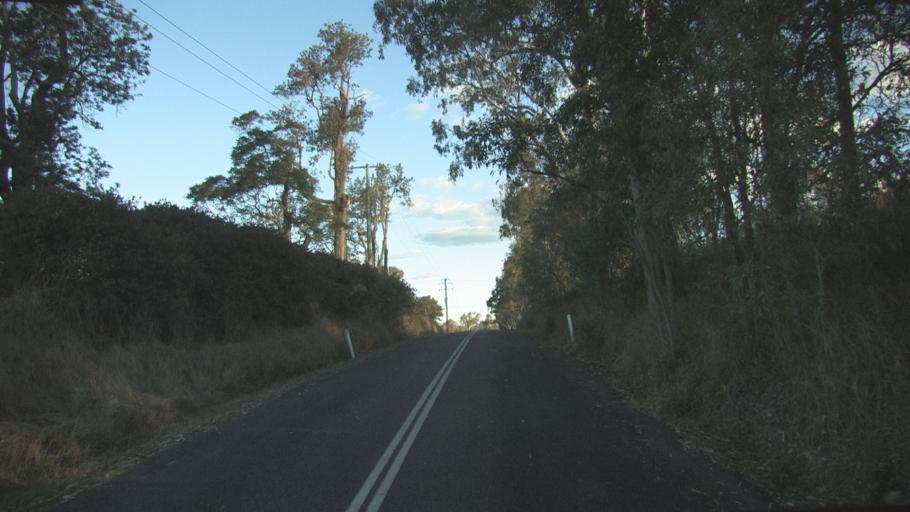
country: AU
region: Queensland
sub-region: Logan
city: Cedar Vale
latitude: -27.8611
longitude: 153.1225
